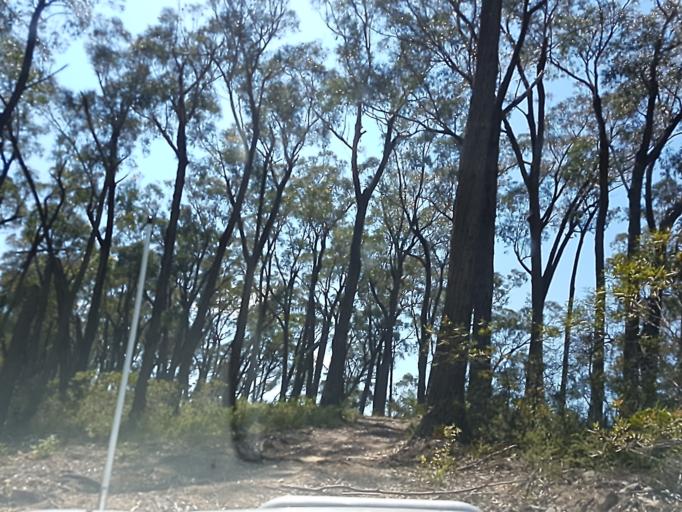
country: AU
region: Victoria
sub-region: East Gippsland
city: Lakes Entrance
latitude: -37.3146
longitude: 148.3418
